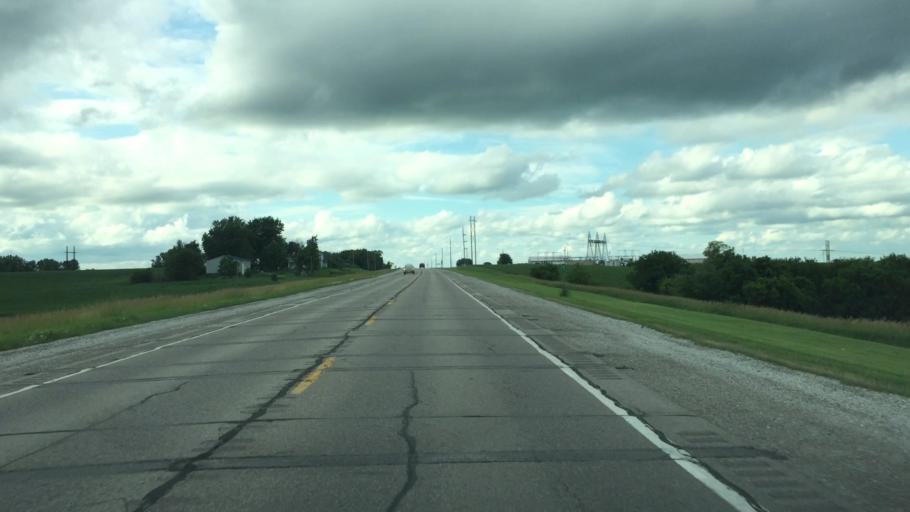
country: US
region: Iowa
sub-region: Jasper County
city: Monroe
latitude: 41.5683
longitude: -93.0969
